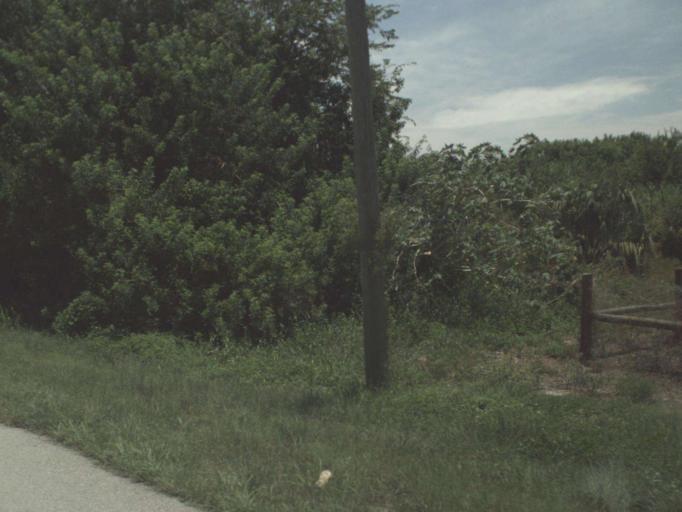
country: US
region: Florida
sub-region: Martin County
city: Indiantown
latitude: 26.9965
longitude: -80.6203
